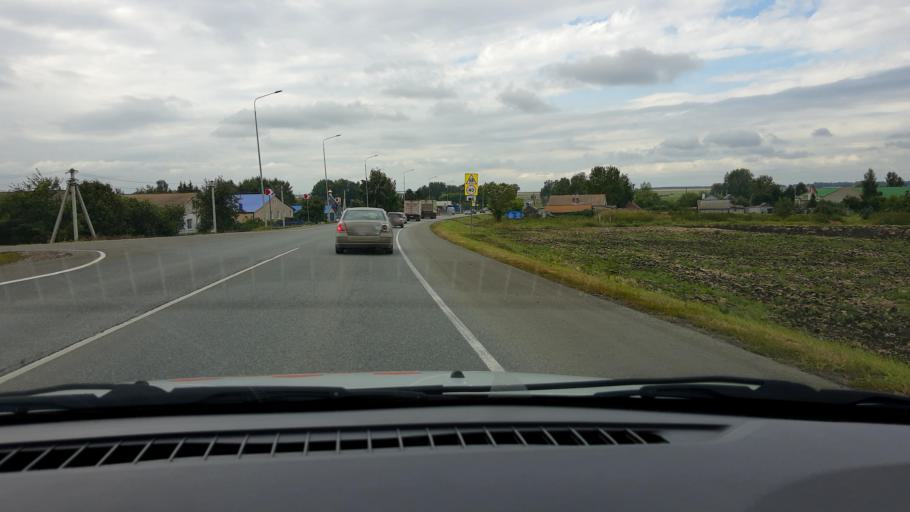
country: RU
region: Tatarstan
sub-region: Alekseyevskiy Rayon
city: Alekseyevskoye
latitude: 55.3089
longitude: 50.3076
